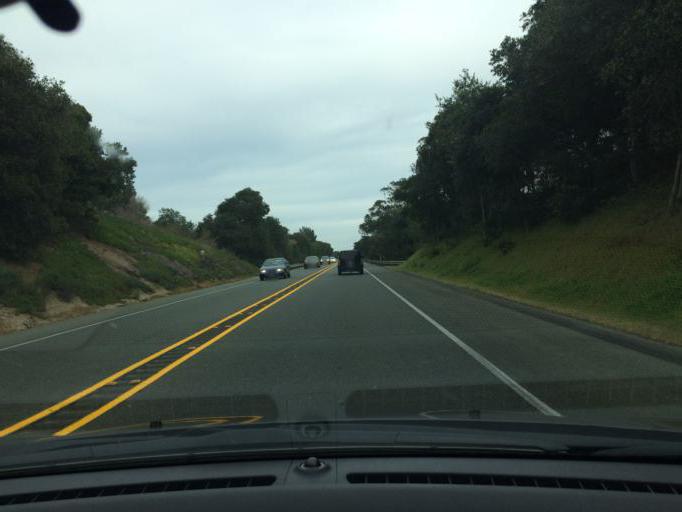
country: US
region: California
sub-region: Monterey County
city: Prunedale
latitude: 36.7784
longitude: -121.7089
